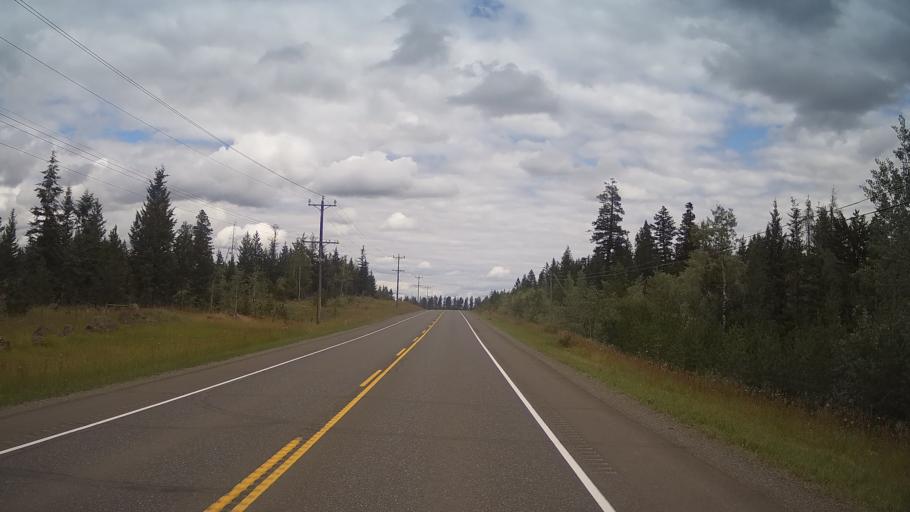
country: CA
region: British Columbia
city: Cache Creek
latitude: 51.2839
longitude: -121.4325
